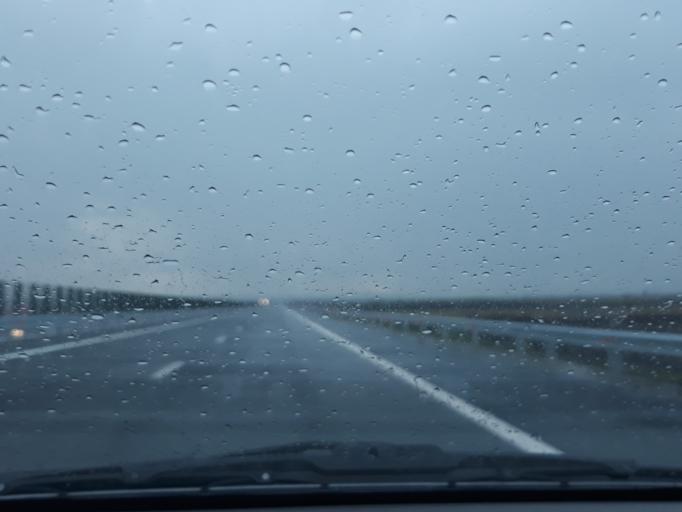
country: RO
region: Mures
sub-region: Comuna Ogra
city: Ogra
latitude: 46.4363
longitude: 24.3104
